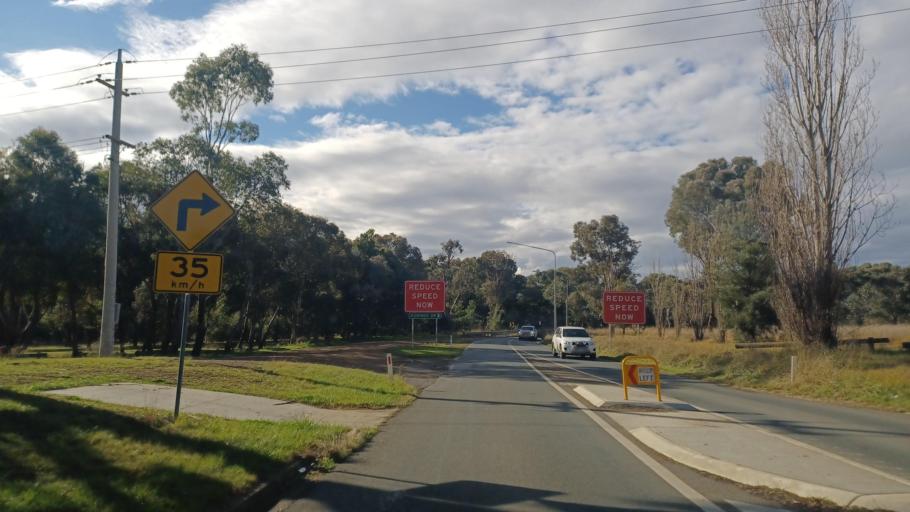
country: AU
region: Australian Capital Territory
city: Belconnen
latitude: -35.1884
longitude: 149.0475
